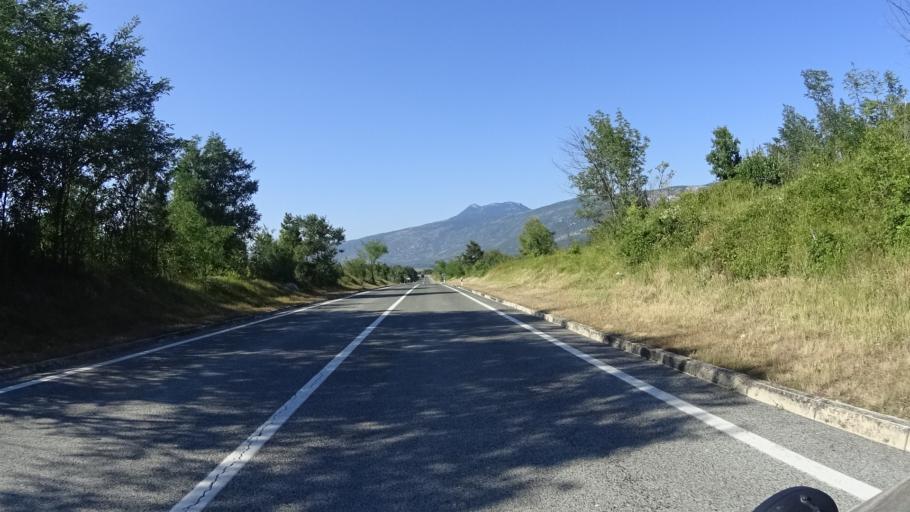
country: HR
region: Istarska
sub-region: Grad Labin
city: Labin
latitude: 45.1685
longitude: 14.1502
